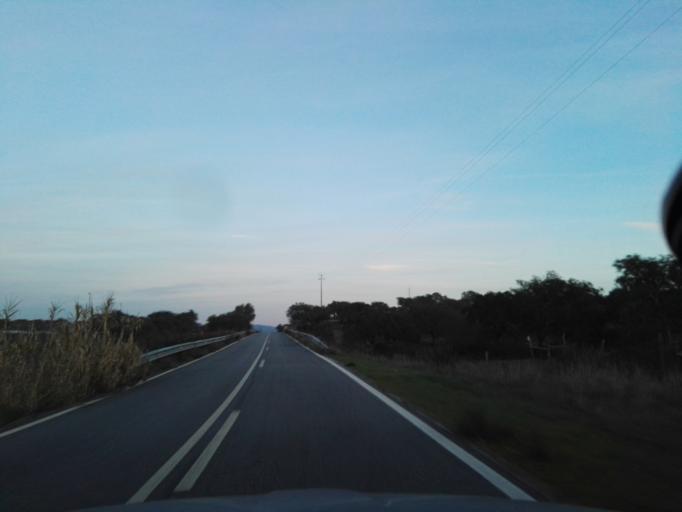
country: PT
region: Evora
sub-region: Montemor-O-Novo
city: Montemor-o-Novo
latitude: 38.7669
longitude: -8.1321
